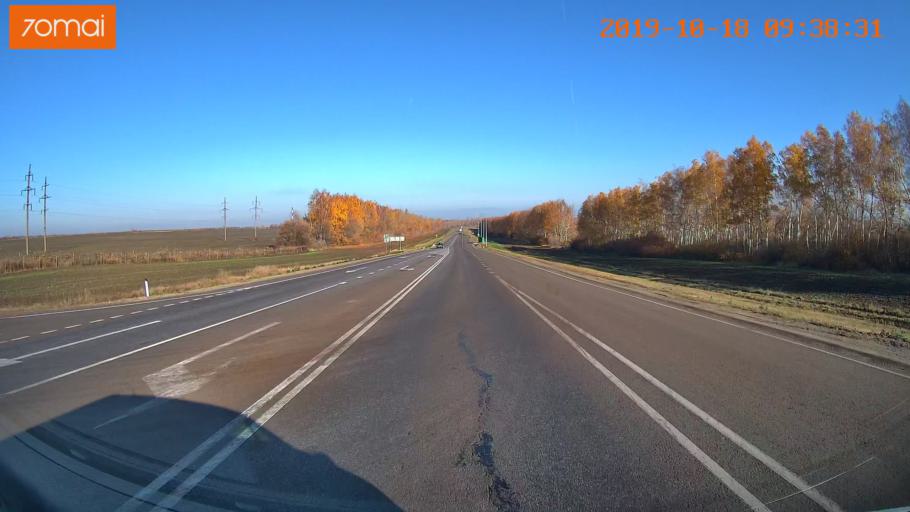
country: RU
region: Tula
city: Yefremov
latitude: 53.2391
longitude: 38.1368
